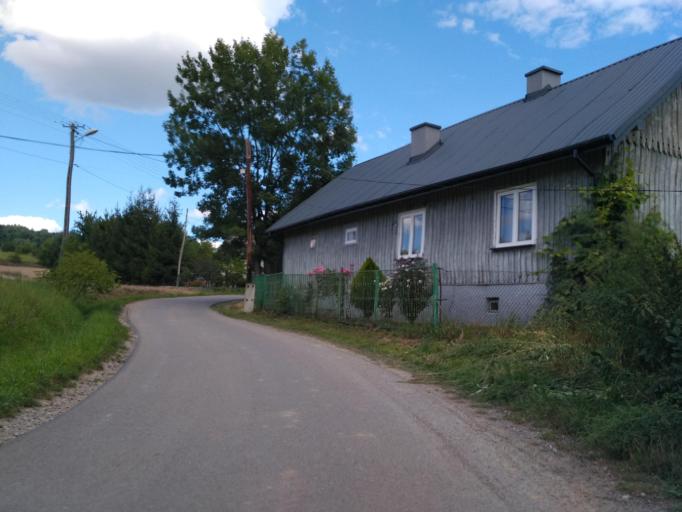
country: PL
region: Subcarpathian Voivodeship
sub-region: Powiat jasielski
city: Tarnowiec
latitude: 49.7662
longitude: 21.5332
